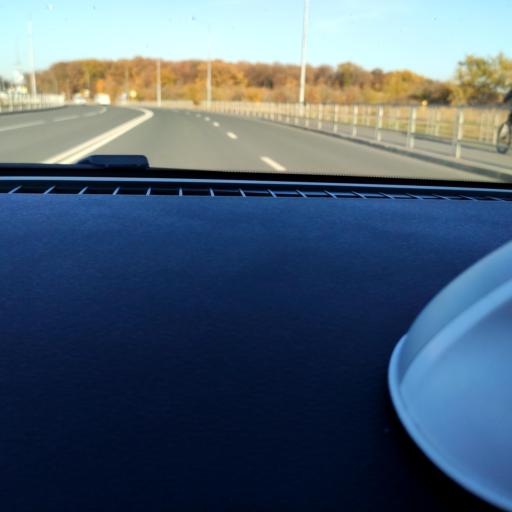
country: RU
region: Samara
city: Samara
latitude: 53.2913
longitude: 50.2384
